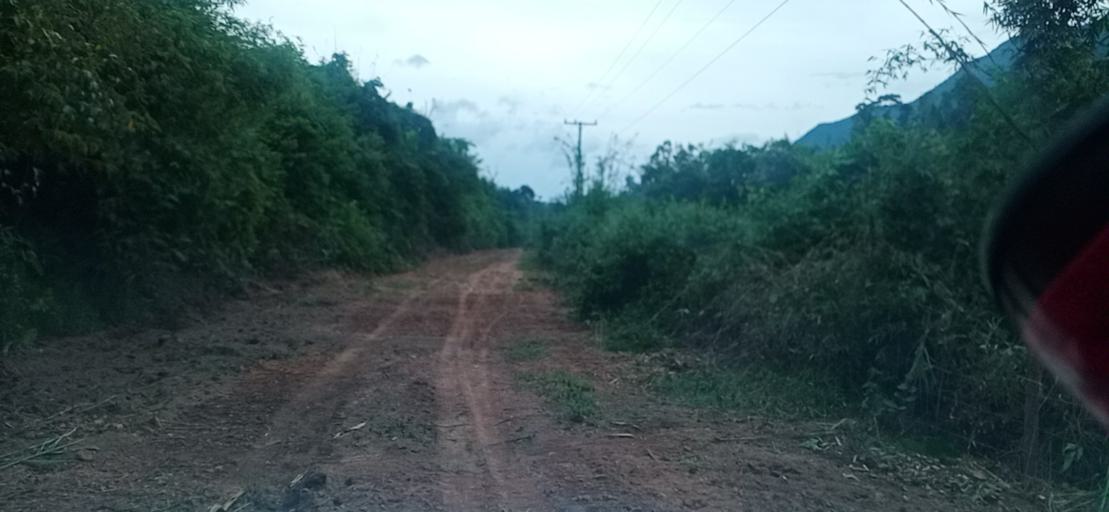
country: TH
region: Changwat Bueng Kan
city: Pak Khat
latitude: 18.5595
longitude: 103.2443
